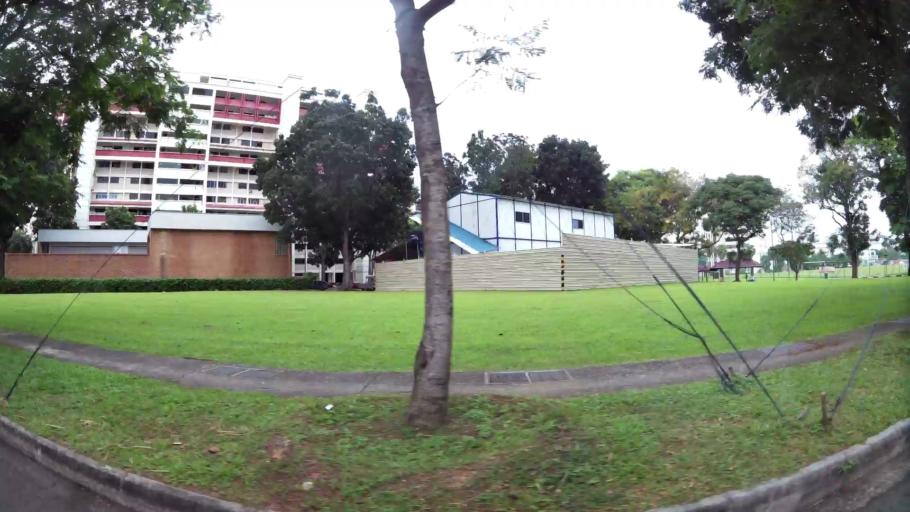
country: SG
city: Singapore
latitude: 1.3649
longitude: 103.8719
